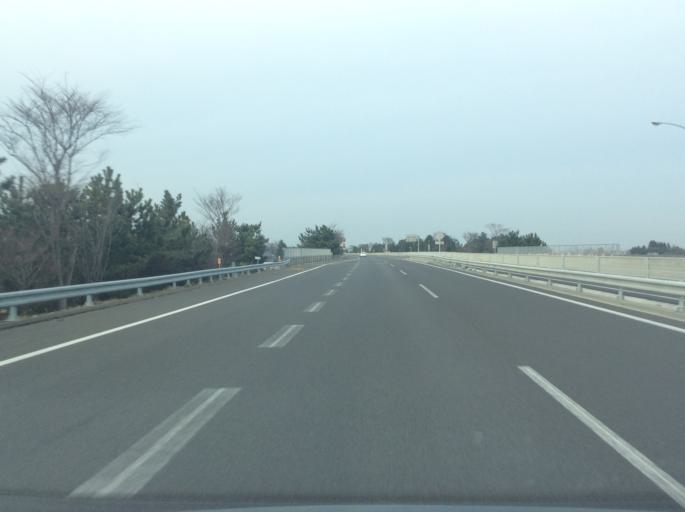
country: JP
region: Miyagi
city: Iwanuma
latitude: 38.1073
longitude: 140.8897
